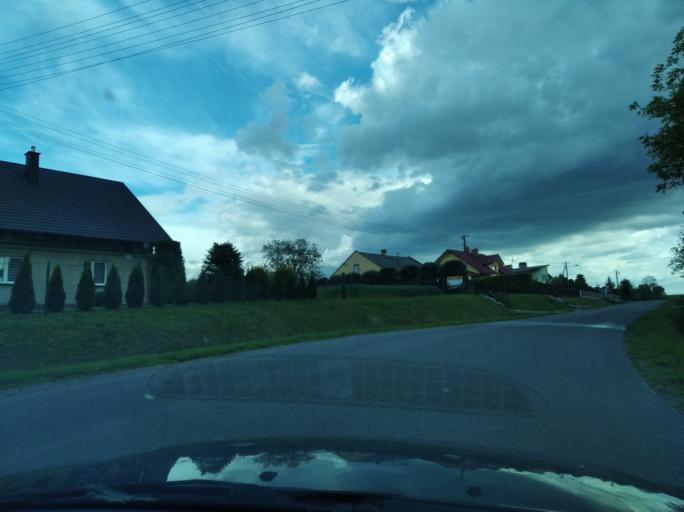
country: PL
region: Subcarpathian Voivodeship
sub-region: Powiat jaroslawski
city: Rokietnica
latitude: 49.9389
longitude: 22.6666
